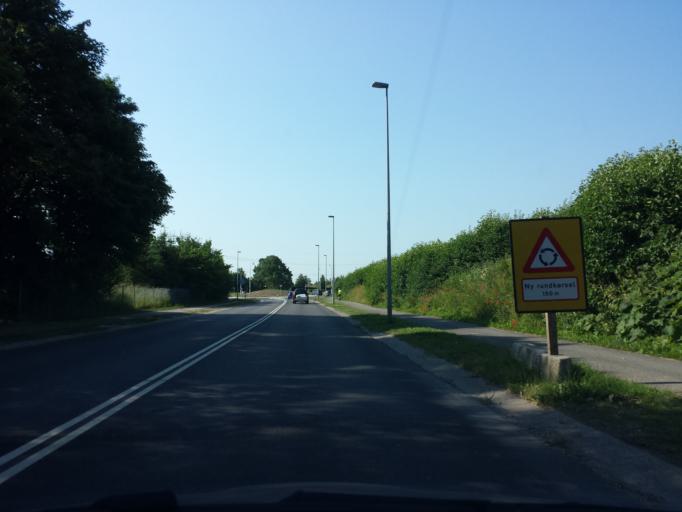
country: DK
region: Capital Region
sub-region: Egedal Kommune
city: Smorumnedre
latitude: 55.7307
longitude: 12.3097
